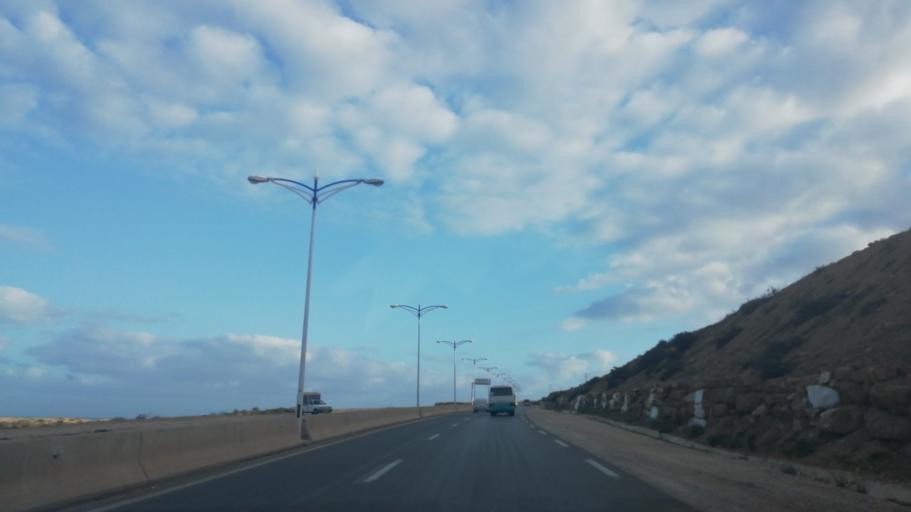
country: DZ
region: Mostaganem
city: Mostaganem
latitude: 36.0379
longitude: 0.1433
